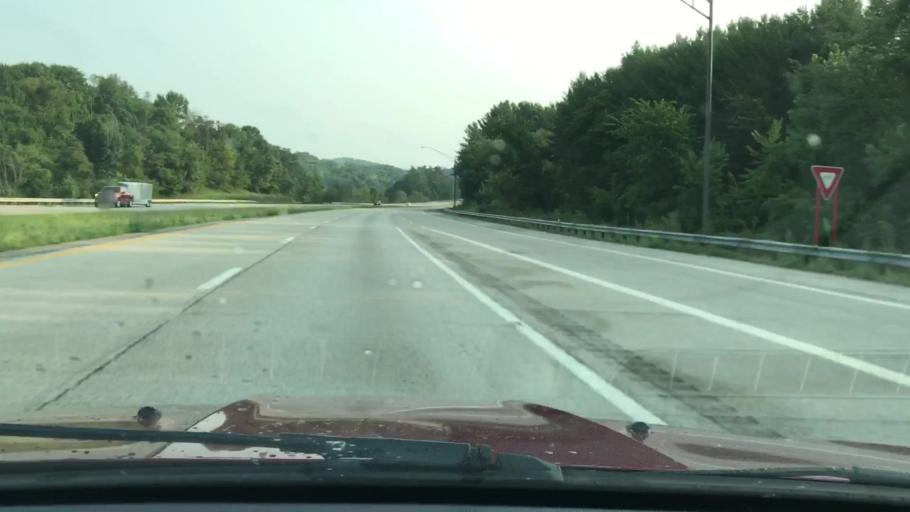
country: US
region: Ohio
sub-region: Washington County
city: Marietta
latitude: 39.4553
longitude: -81.4396
